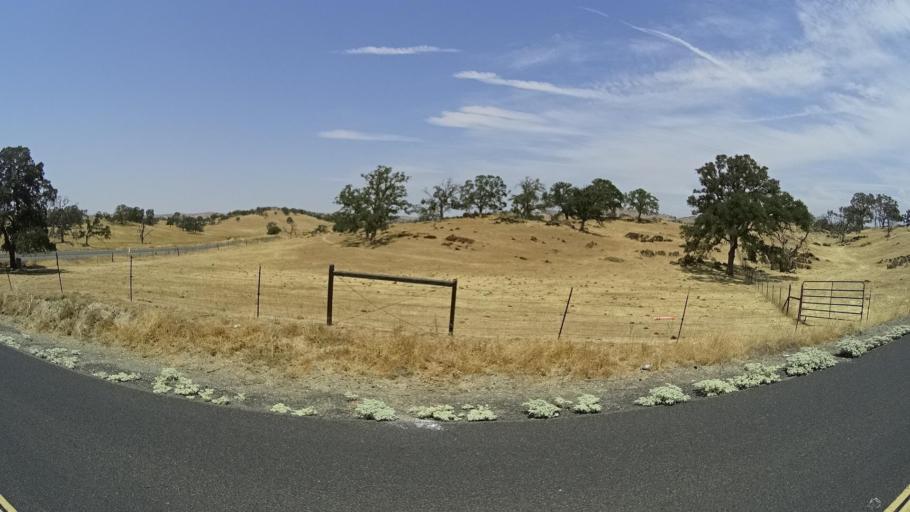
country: US
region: California
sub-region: Tuolumne County
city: Jamestown
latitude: 37.6299
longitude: -120.3710
